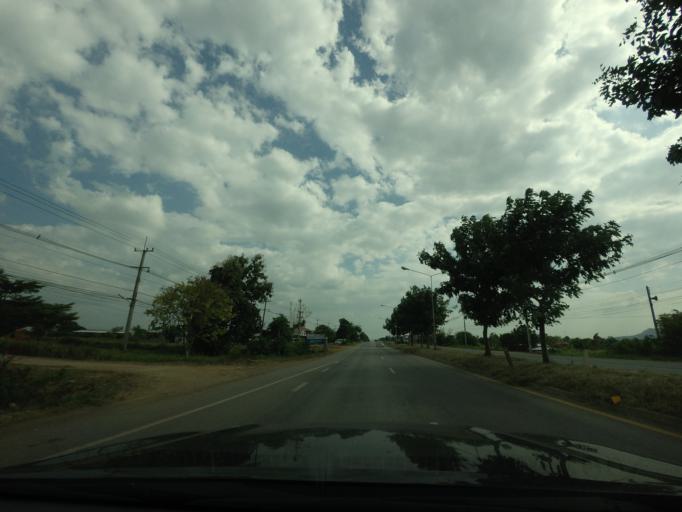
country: TH
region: Lop Buri
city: Chai Badan
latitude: 15.2537
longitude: 101.1254
